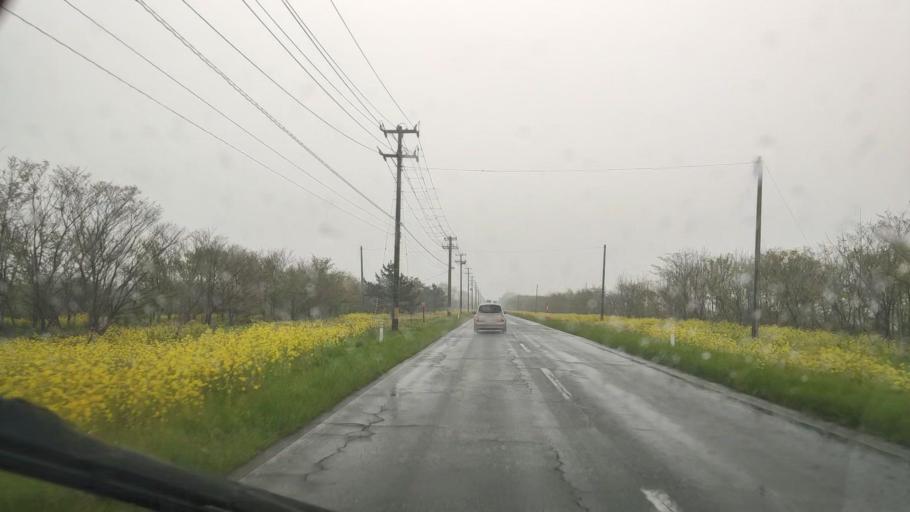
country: JP
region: Akita
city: Tenno
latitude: 39.9961
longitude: 139.9463
